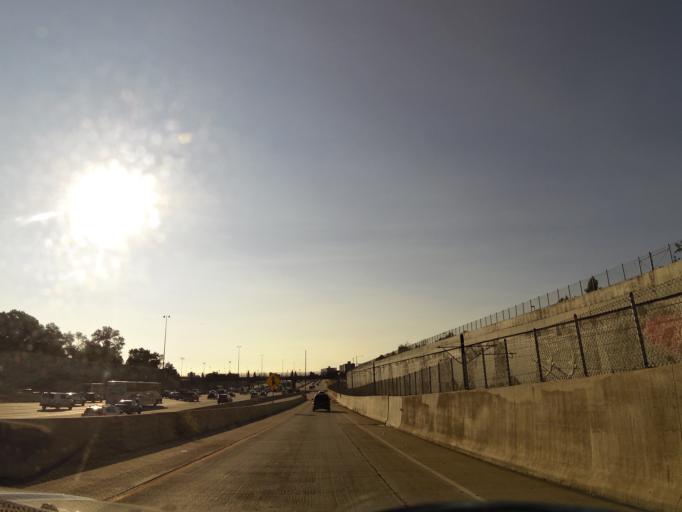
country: US
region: Colorado
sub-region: Arapahoe County
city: Glendale
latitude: 39.6886
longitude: -104.9721
